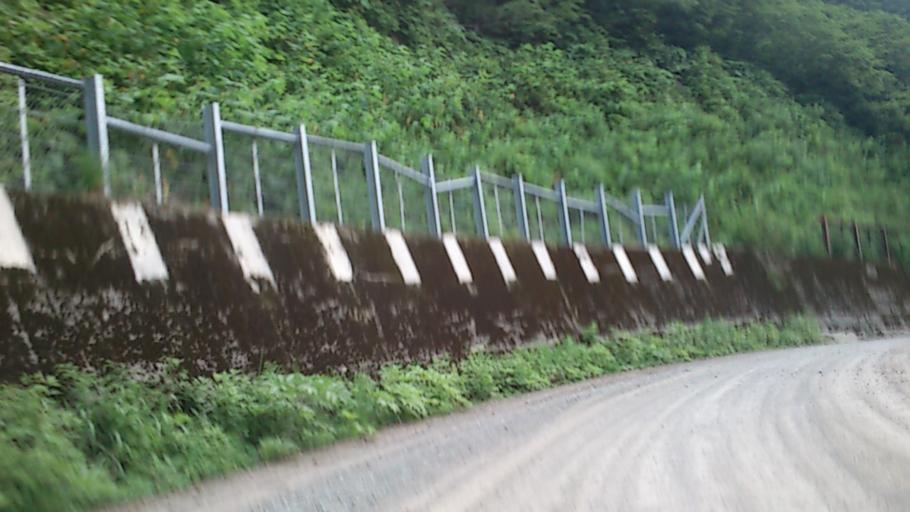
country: JP
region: Aomori
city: Hirosaki
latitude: 40.5263
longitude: 140.1791
